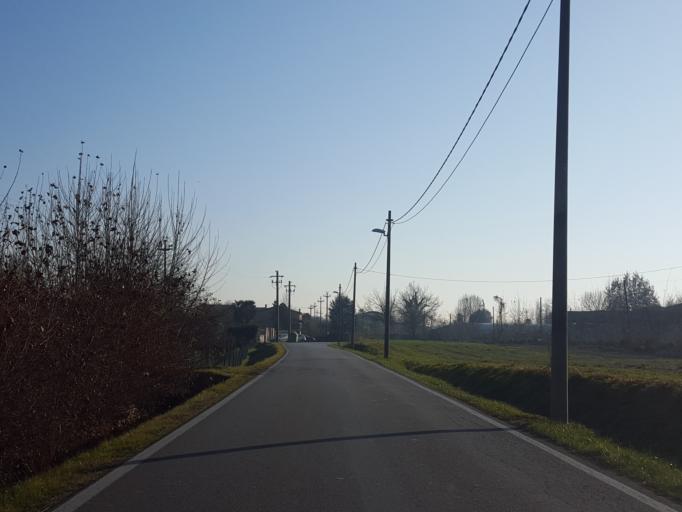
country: IT
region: Veneto
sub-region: Provincia di Vicenza
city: Villaggio Montegrappa
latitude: 45.5509
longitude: 11.6038
